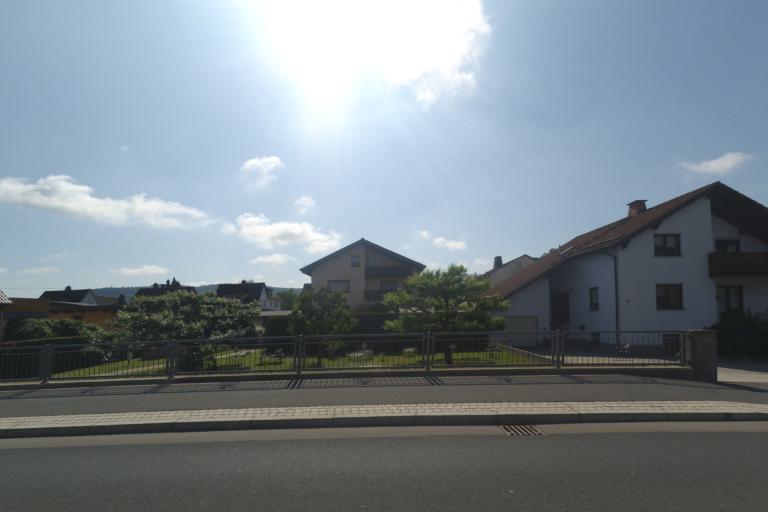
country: DE
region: Bavaria
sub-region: Upper Franconia
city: Stockheim
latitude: 50.3177
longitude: 11.2812
